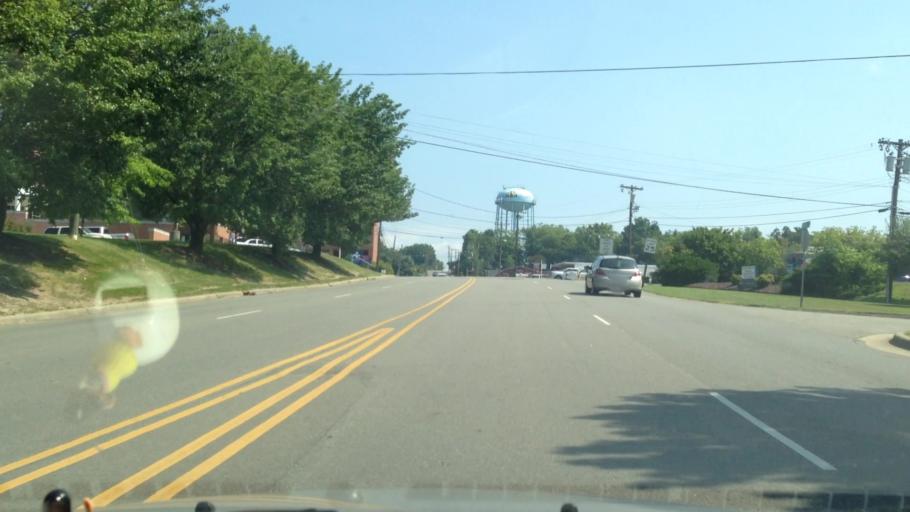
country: US
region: North Carolina
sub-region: Surry County
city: Mount Airy
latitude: 36.4871
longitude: -80.6115
